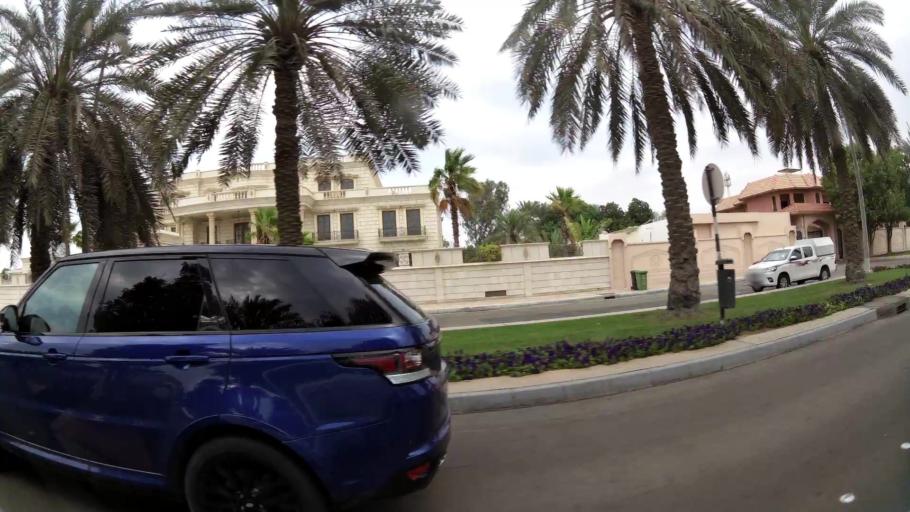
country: AE
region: Abu Dhabi
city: Abu Dhabi
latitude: 24.4419
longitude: 54.3602
